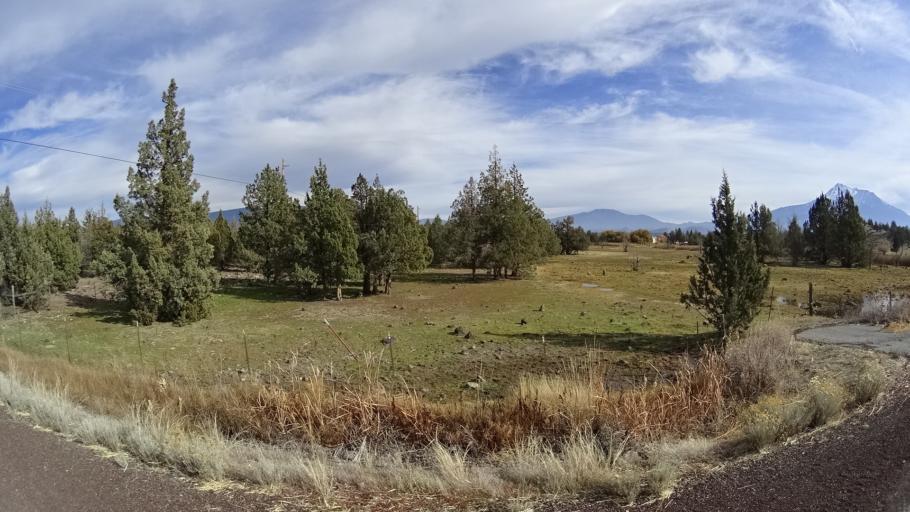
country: US
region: California
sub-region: Siskiyou County
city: Weed
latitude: 41.5825
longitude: -122.3996
